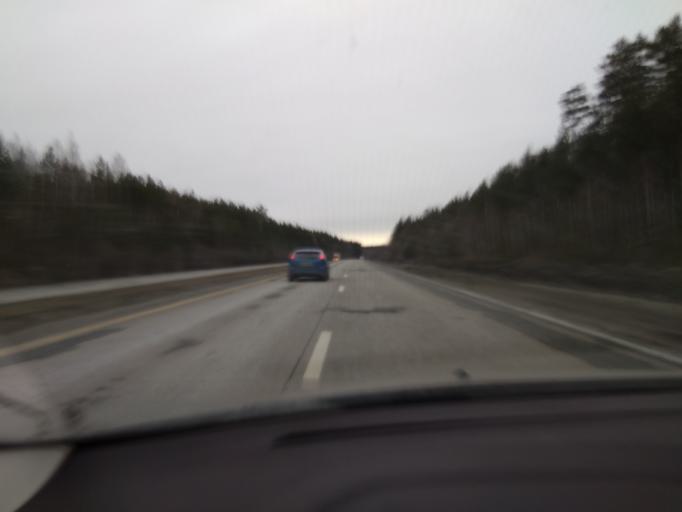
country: RU
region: Sverdlovsk
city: Shchelkun
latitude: 56.2961
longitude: 60.8686
